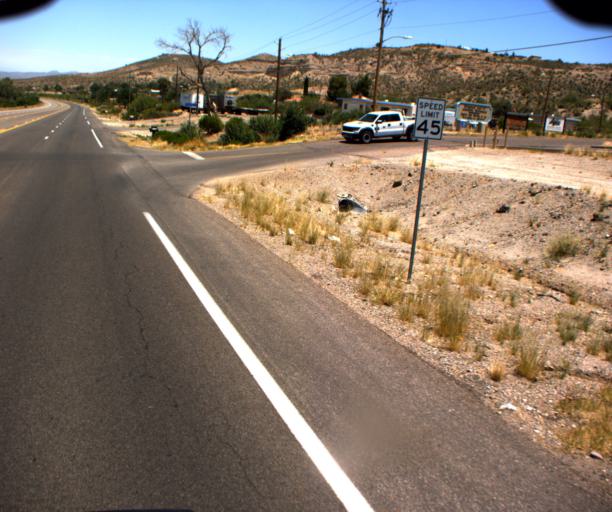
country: US
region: Arizona
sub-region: Gila County
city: Claypool
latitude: 33.4203
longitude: -110.8257
